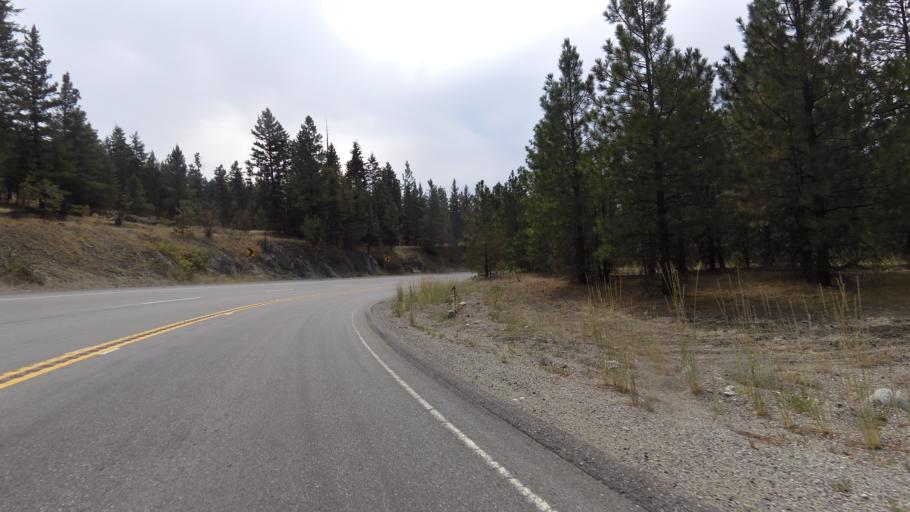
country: CA
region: British Columbia
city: Osoyoos
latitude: 49.0139
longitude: -119.3671
